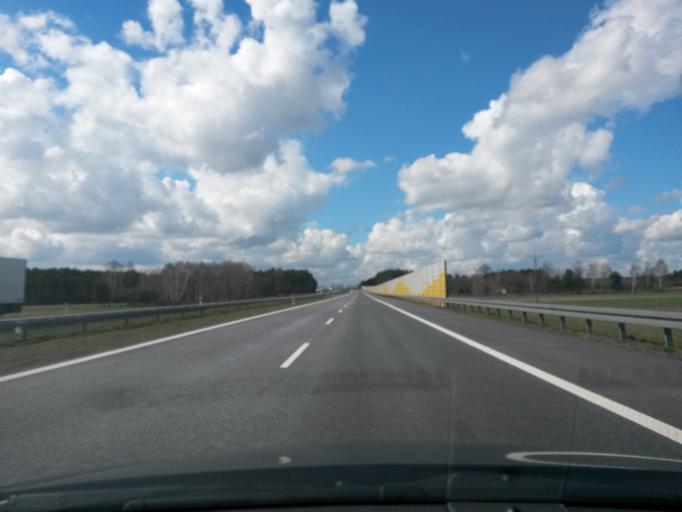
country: PL
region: Lodz Voivodeship
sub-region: Powiat leczycki
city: Swinice Warckie
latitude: 52.0226
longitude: 18.9269
